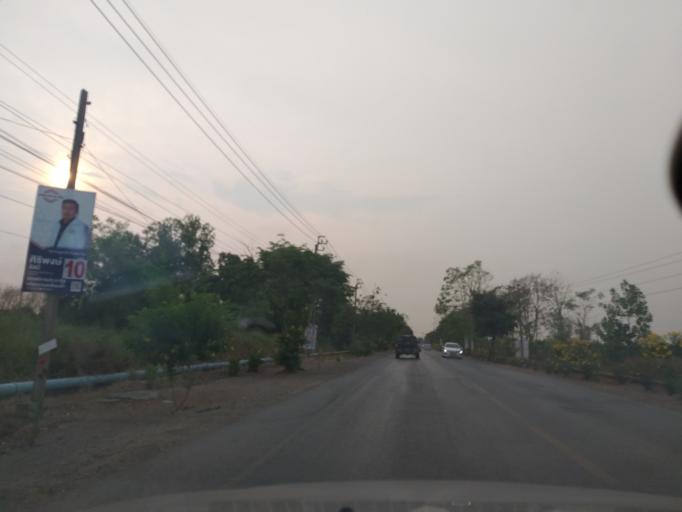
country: TH
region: Bangkok
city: Nong Chok
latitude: 13.8367
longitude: 100.9055
